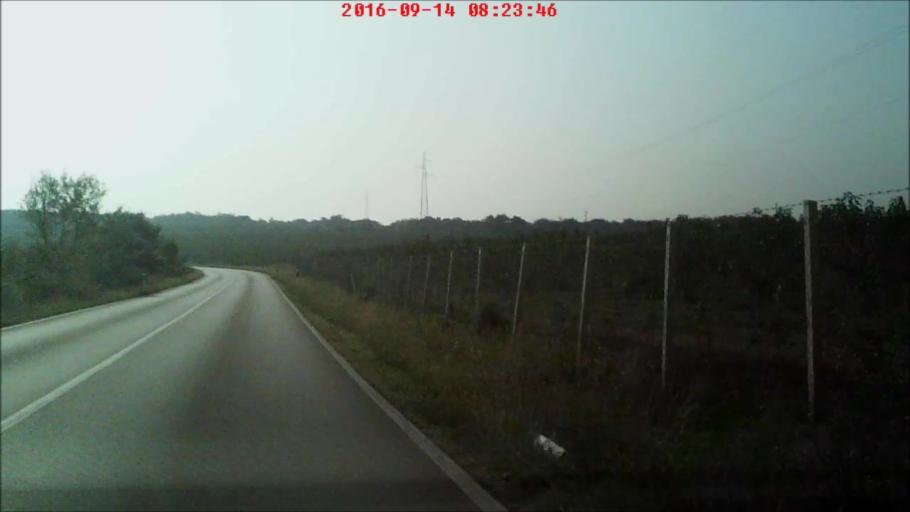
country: HR
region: Zadarska
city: Vrsi
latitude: 44.2102
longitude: 15.2353
